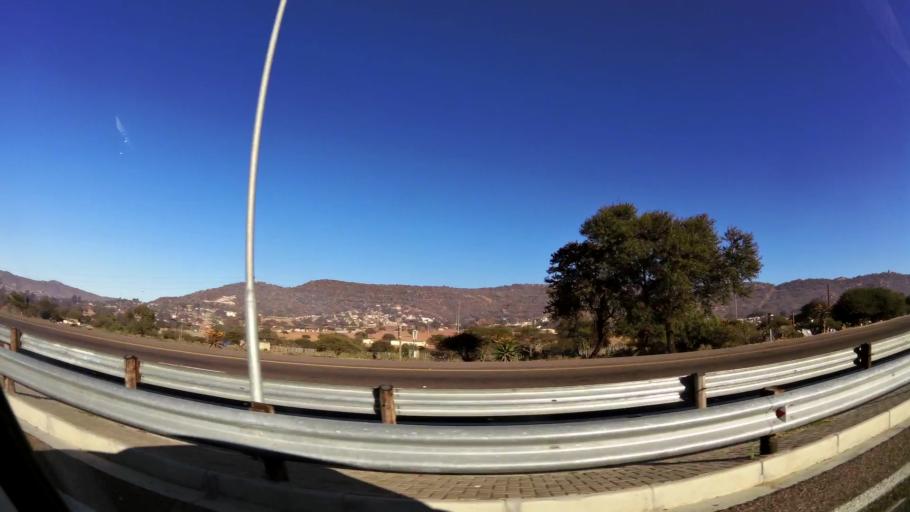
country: ZA
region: Limpopo
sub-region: Capricorn District Municipality
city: Mankoeng
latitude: -23.9388
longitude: 29.7947
